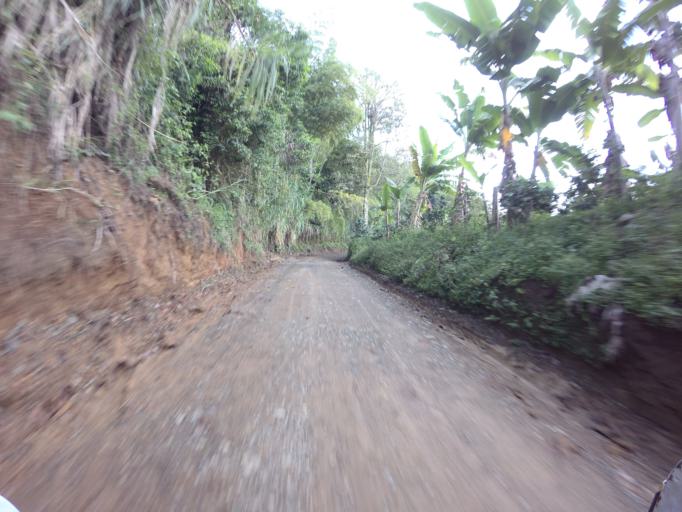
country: CO
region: Valle del Cauca
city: Ulloa
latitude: 4.7077
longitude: -75.7099
